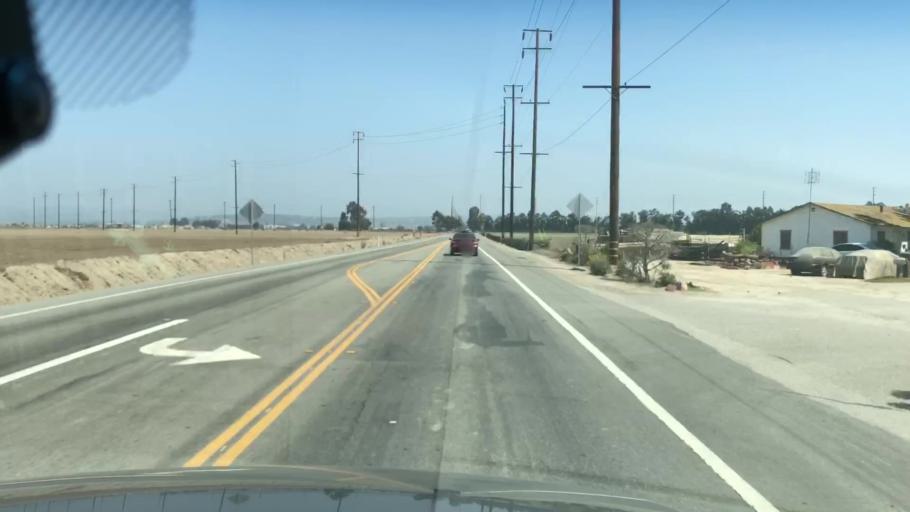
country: US
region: California
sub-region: Ventura County
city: Oxnard
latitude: 34.1770
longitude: -119.1228
